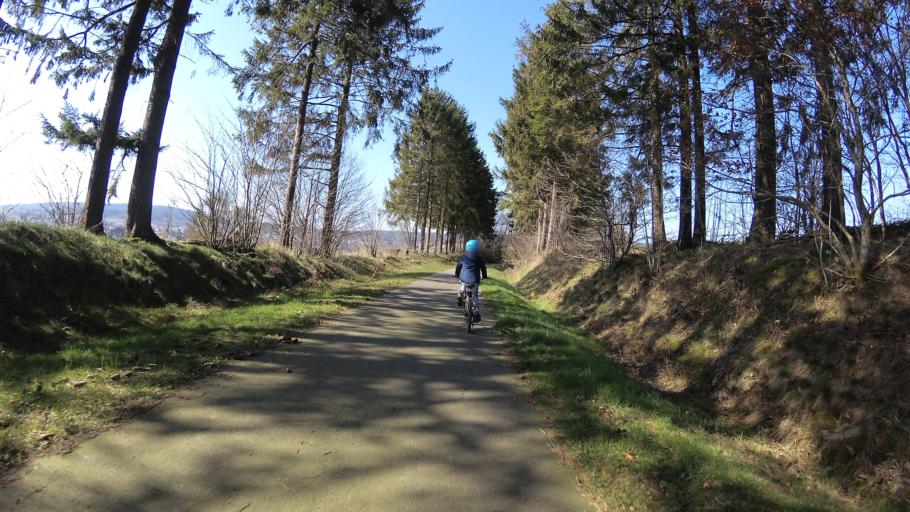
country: DE
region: Rheinland-Pfalz
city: Reinsfeld
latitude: 49.6743
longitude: 6.8908
